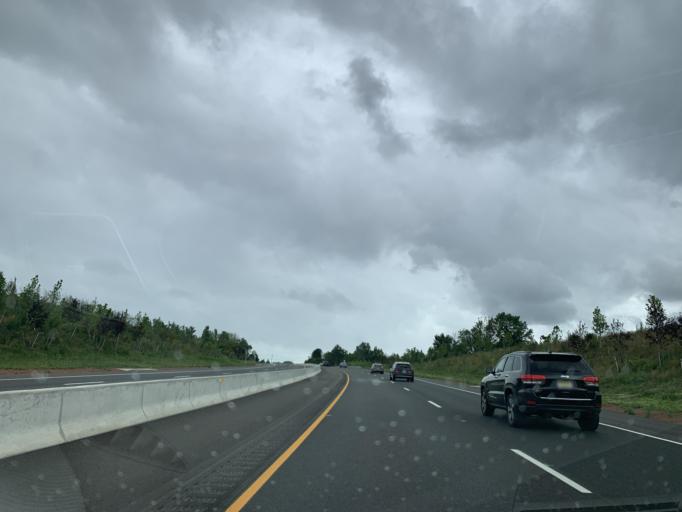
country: US
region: New Jersey
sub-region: Somerset County
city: Bloomingdale
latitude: 40.5059
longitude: -74.6350
